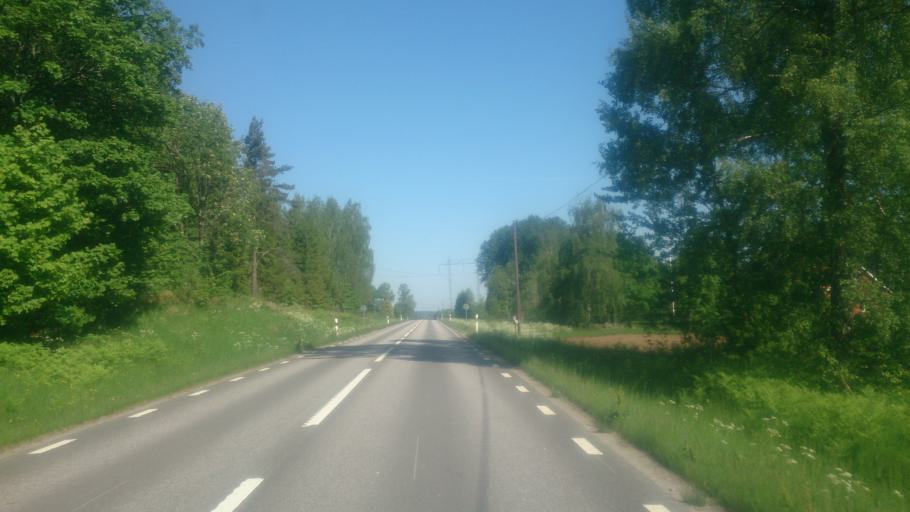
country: SE
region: OEstergoetland
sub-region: Atvidabergs Kommun
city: Atvidaberg
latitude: 58.1488
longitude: 16.0752
